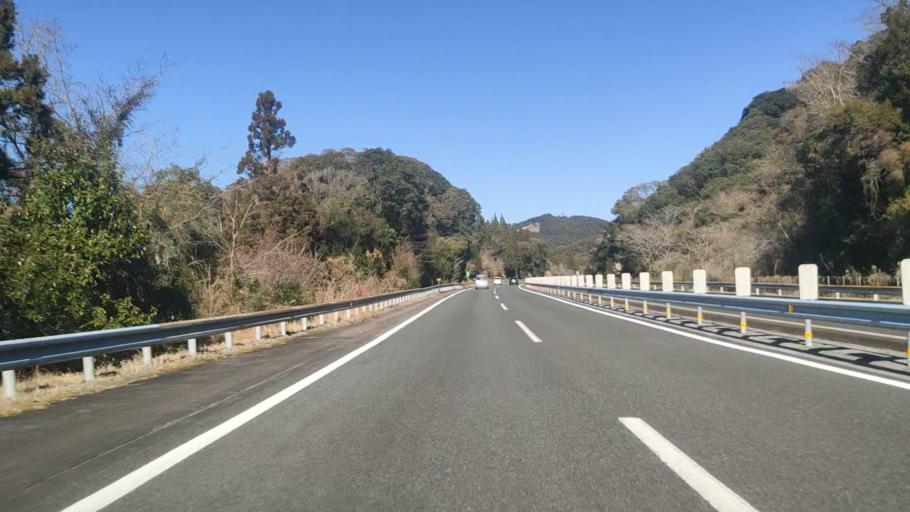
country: JP
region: Miyazaki
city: Miyakonojo
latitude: 31.8155
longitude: 131.2159
